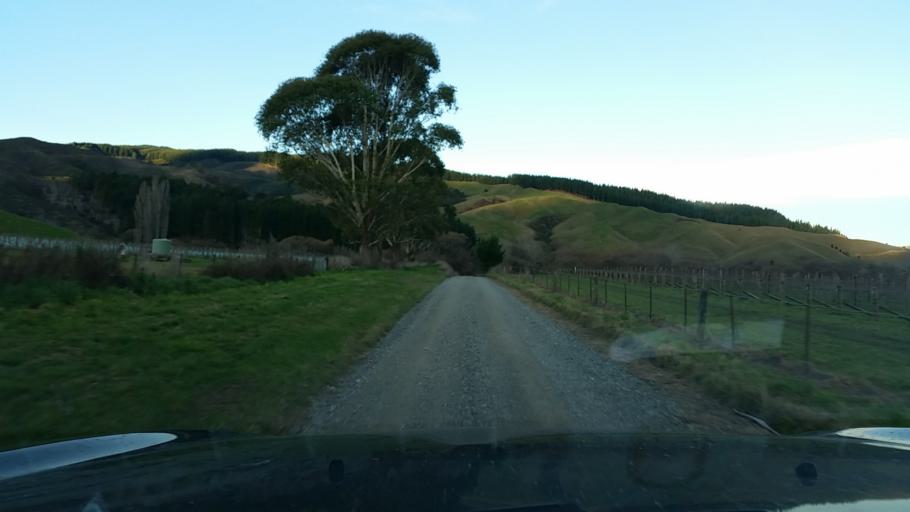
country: NZ
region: Marlborough
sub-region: Marlborough District
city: Blenheim
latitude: -41.5138
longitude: 173.5881
